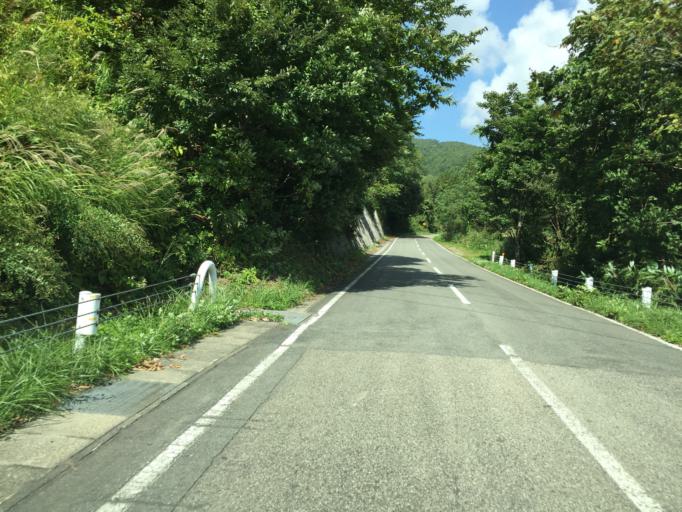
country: JP
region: Fukushima
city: Inawashiro
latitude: 37.5873
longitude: 140.0300
